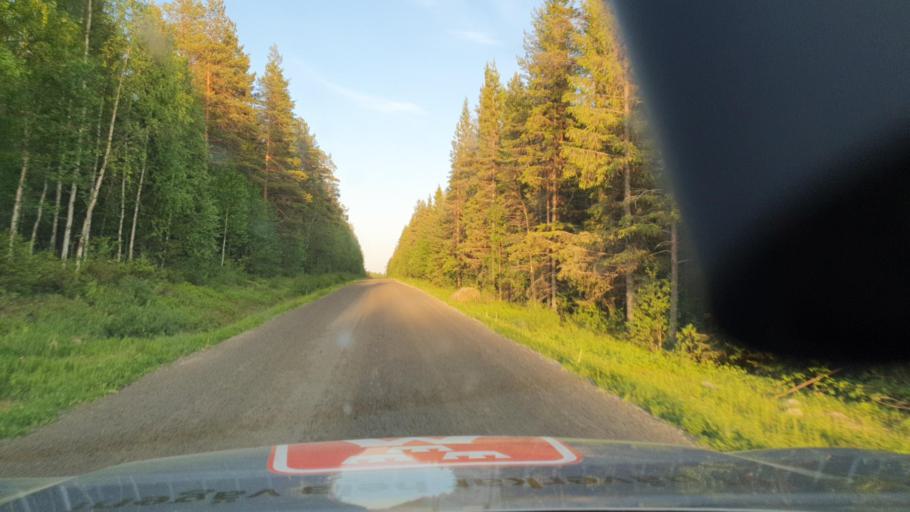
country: SE
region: Norrbotten
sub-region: Bodens Kommun
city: Boden
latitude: 66.0657
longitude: 21.7211
